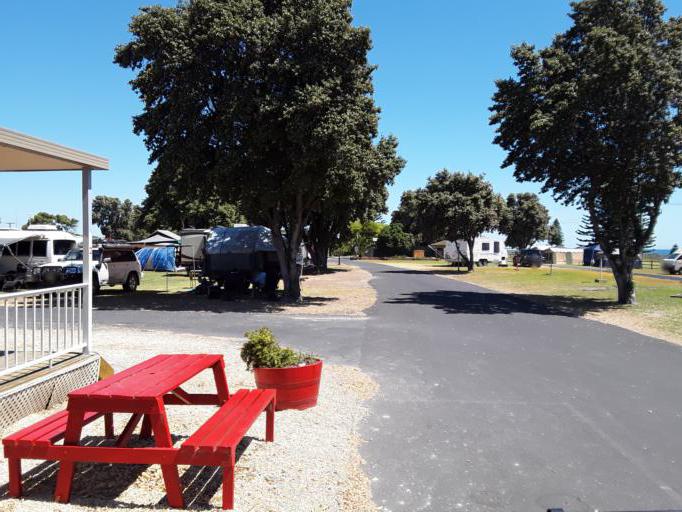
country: AU
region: South Australia
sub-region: Tatiara
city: Keith
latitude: -36.8367
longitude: 139.8458
